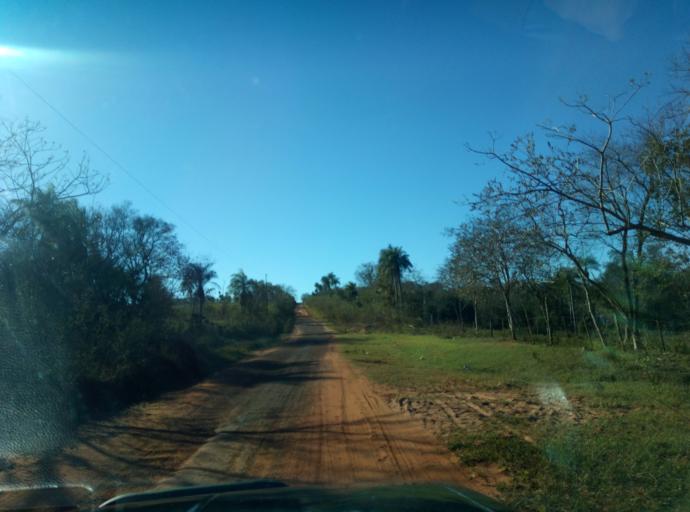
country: PY
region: Caaguazu
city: Carayao
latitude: -25.1573
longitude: -56.2994
